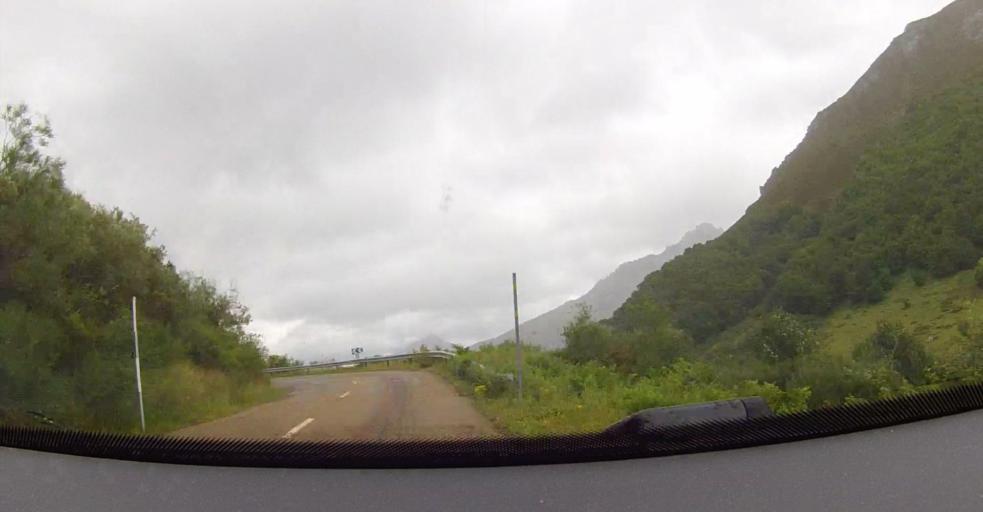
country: ES
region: Castille and Leon
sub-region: Provincia de Leon
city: Puebla de Lillo
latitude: 43.0606
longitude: -5.2786
